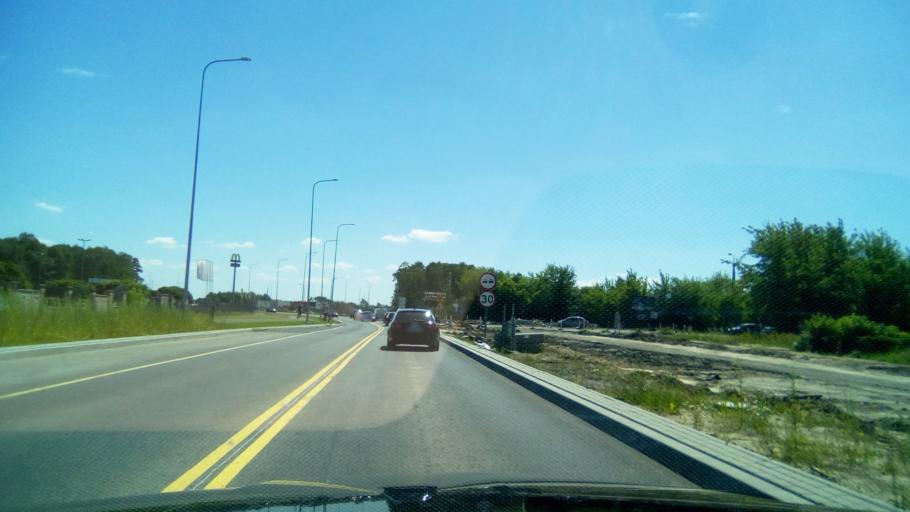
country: PL
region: Masovian Voivodeship
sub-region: Radom
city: Radom
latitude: 51.4152
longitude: 21.1996
